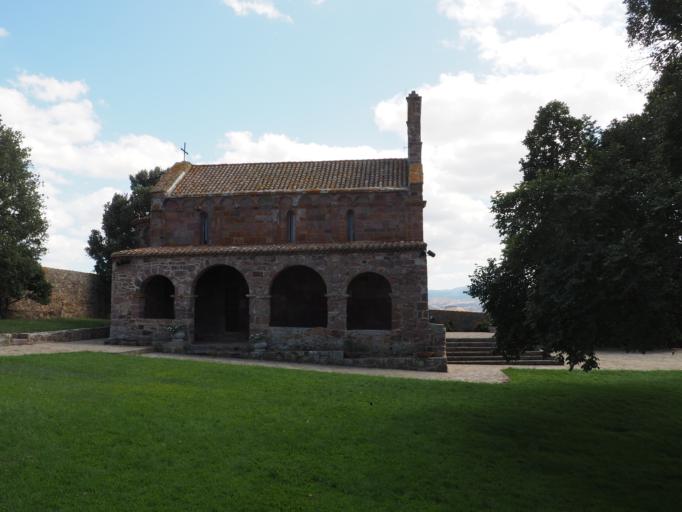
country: IT
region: Sardinia
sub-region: Provincia di Olbia-Tempio
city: Oschiri
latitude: 40.7129
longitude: 9.0482
